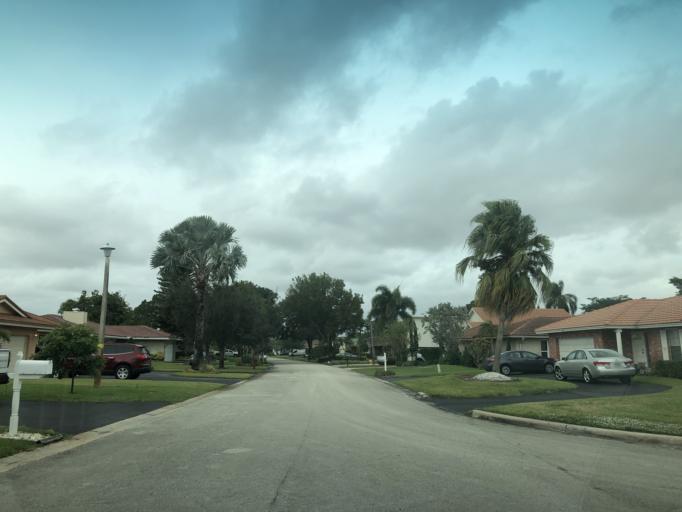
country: US
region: Florida
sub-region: Broward County
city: North Lauderdale
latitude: 26.2412
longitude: -80.2367
